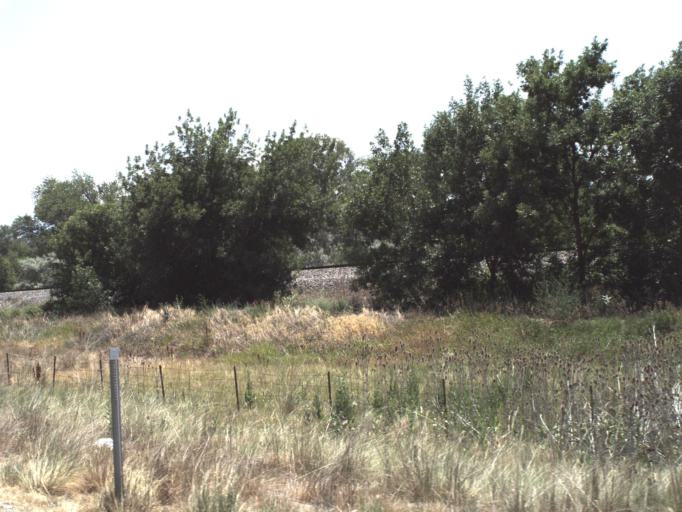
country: US
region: Utah
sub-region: Weber County
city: Marriott-Slaterville
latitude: 41.2445
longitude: -112.0446
